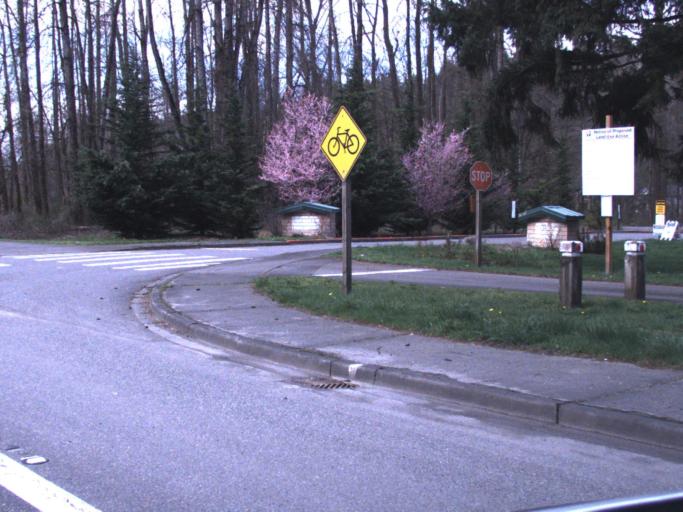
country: US
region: Washington
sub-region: King County
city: East Renton Highlands
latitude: 47.4631
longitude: -122.1112
